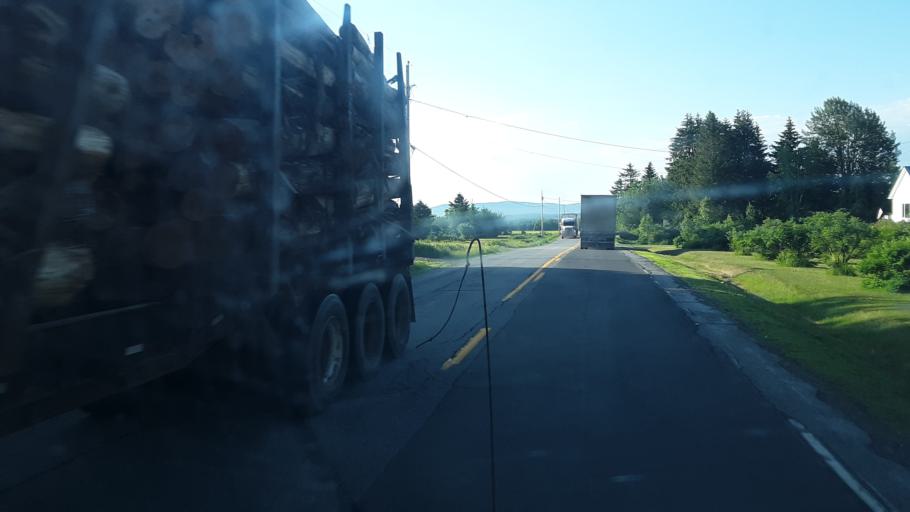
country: US
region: Maine
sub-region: Penobscot County
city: Patten
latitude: 46.1714
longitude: -68.2378
